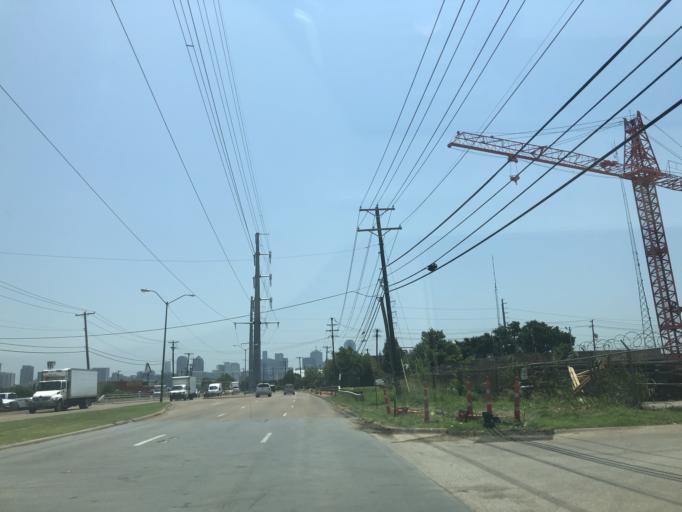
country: US
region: Texas
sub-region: Dallas County
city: Dallas
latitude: 32.7969
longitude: -96.8371
